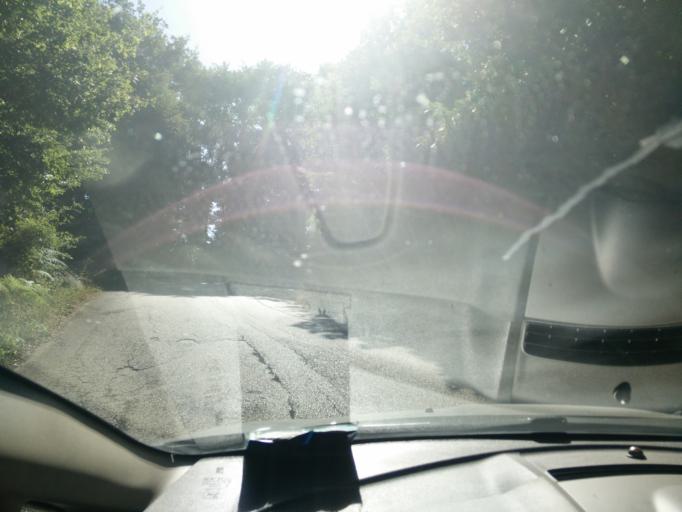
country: IT
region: Apulia
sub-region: Provincia di Foggia
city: Monte Sant'Angelo
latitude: 41.7718
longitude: 15.9858
